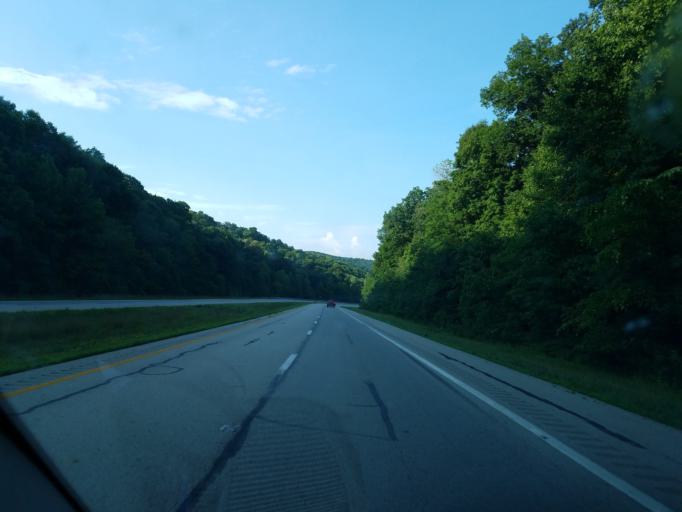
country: US
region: Ohio
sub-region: Adams County
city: Peebles
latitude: 39.0285
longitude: -83.2677
